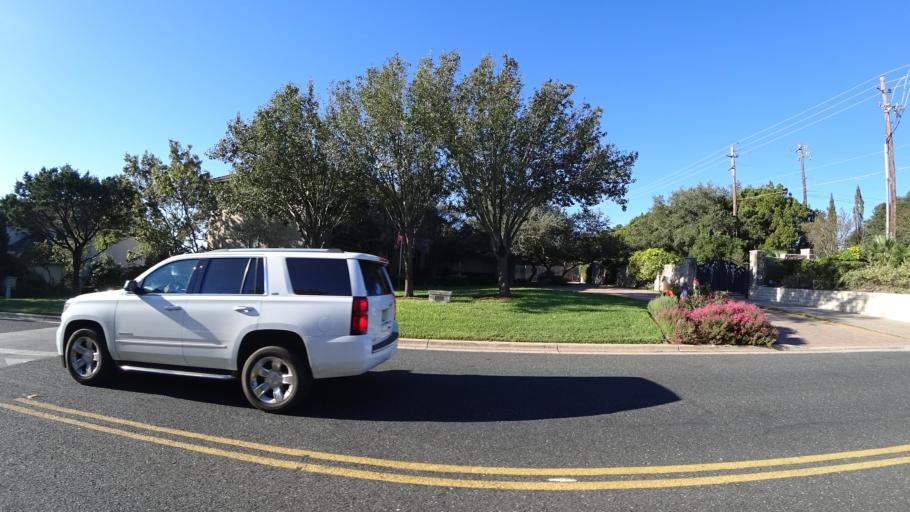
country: US
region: Texas
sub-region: Travis County
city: West Lake Hills
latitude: 30.3596
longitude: -97.8052
